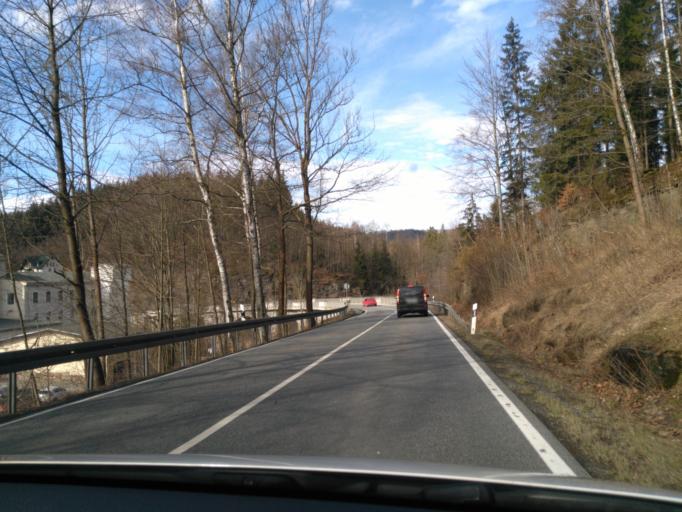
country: DE
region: Saxony
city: Wolkenstein
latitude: 50.6682
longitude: 13.0669
